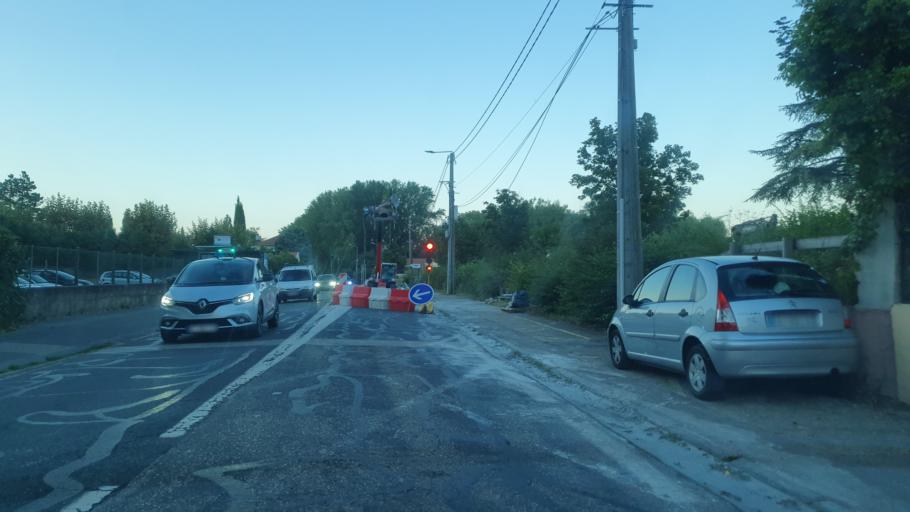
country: FR
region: Rhone-Alpes
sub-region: Departement du Rhone
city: Albigny-sur-Saone
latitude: 45.8558
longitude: 4.8346
